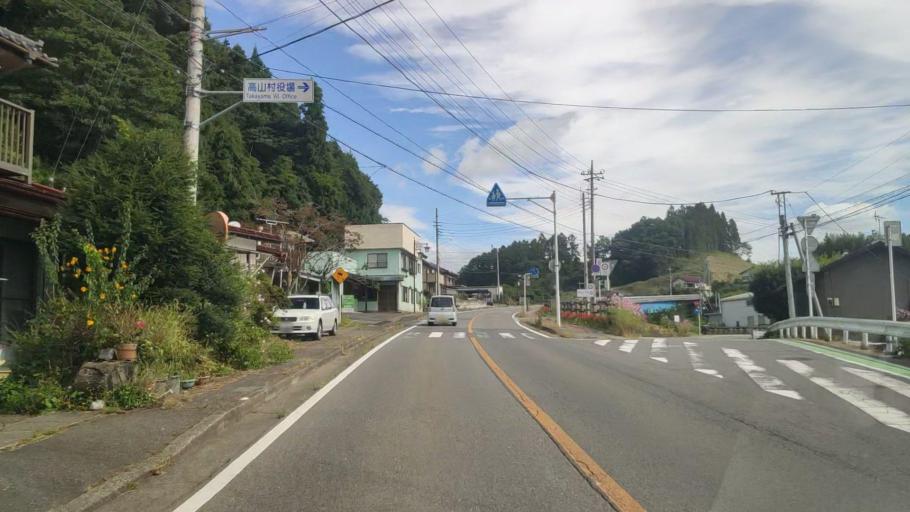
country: JP
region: Gunma
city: Nakanojomachi
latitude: 36.6212
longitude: 138.9410
